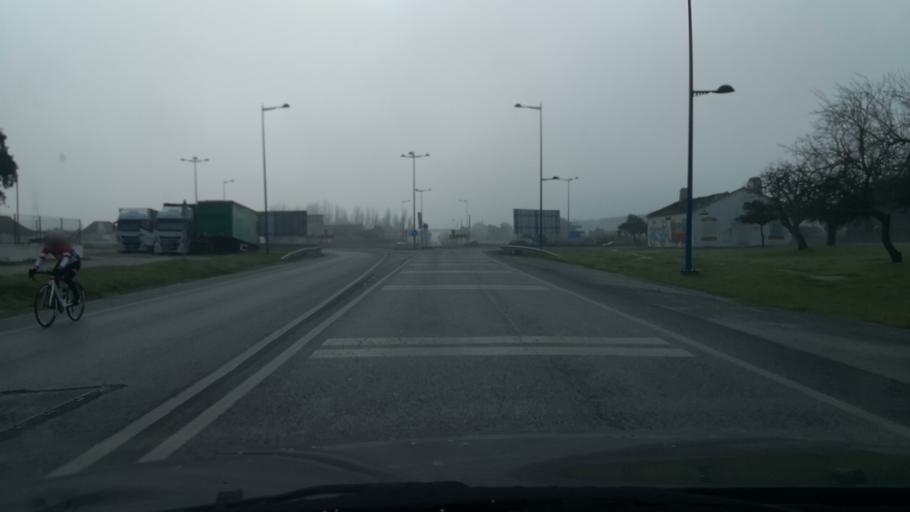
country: PT
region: Setubal
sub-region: Montijo
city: Montijo
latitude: 38.6874
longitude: -8.9451
